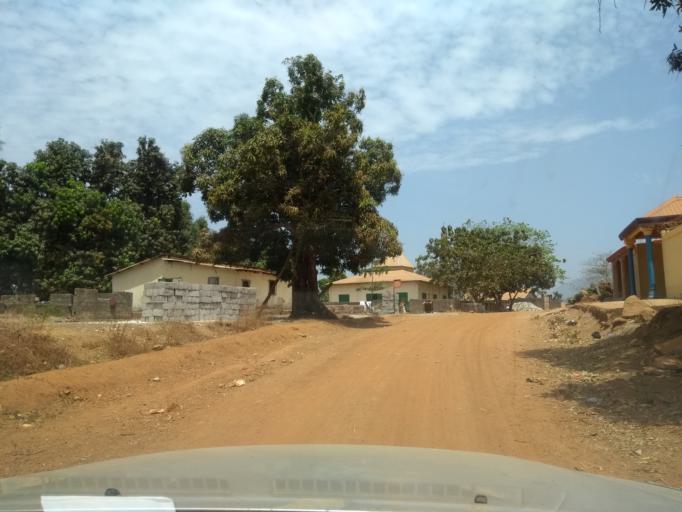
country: GN
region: Kindia
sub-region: Prefecture de Dubreka
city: Dubreka
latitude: 9.7866
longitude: -13.5416
